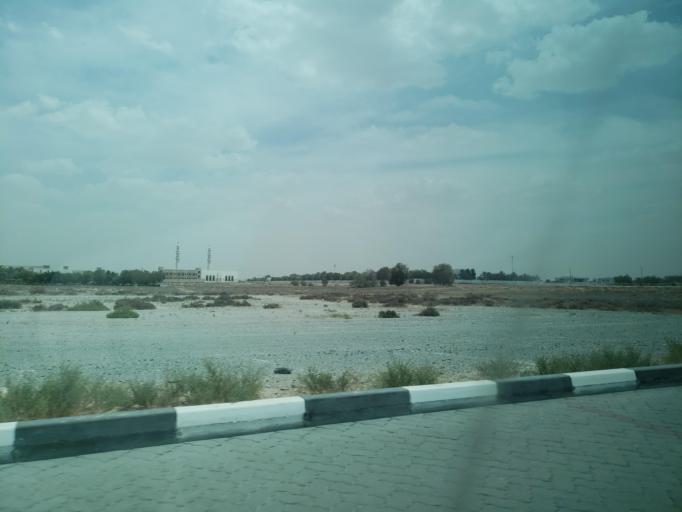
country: AE
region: Ash Shariqah
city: Sharjah
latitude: 25.3182
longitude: 55.5086
